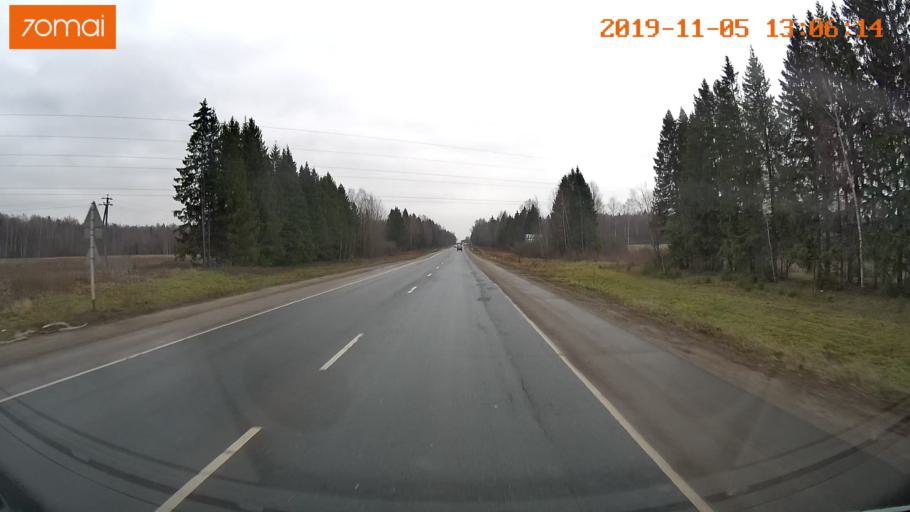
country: RU
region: Ivanovo
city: Kitovo
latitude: 56.8770
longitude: 41.2598
